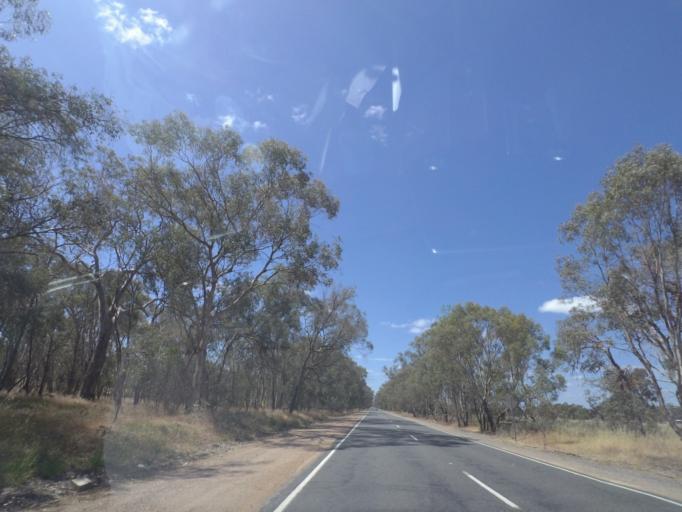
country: AU
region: Victoria
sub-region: Wangaratta
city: Wangaratta
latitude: -36.4371
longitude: 146.2487
